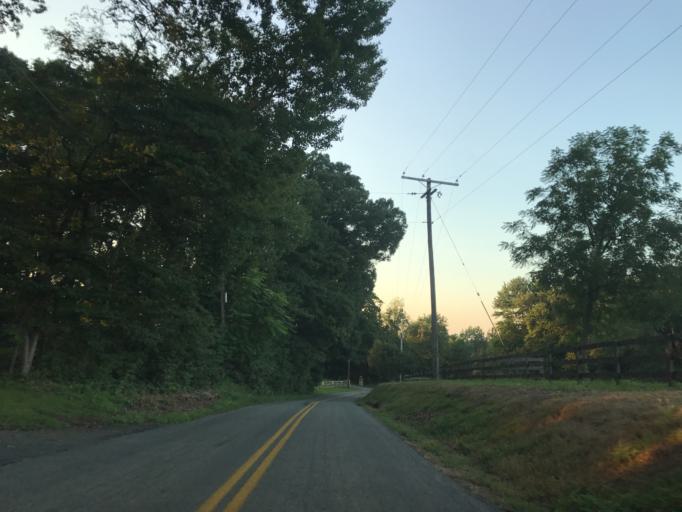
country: US
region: Maryland
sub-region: Harford County
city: Jarrettsville
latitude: 39.6284
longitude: -76.5214
